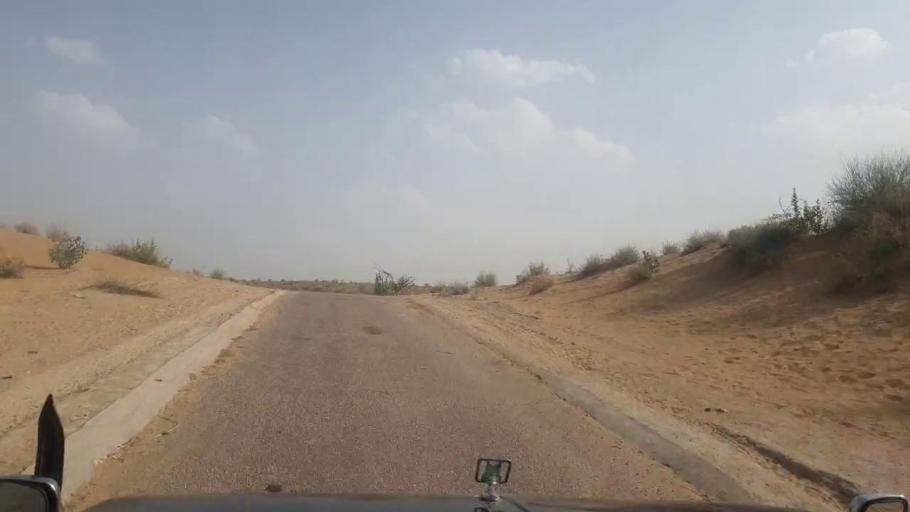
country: PK
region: Sindh
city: Islamkot
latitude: 25.1404
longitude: 70.3171
